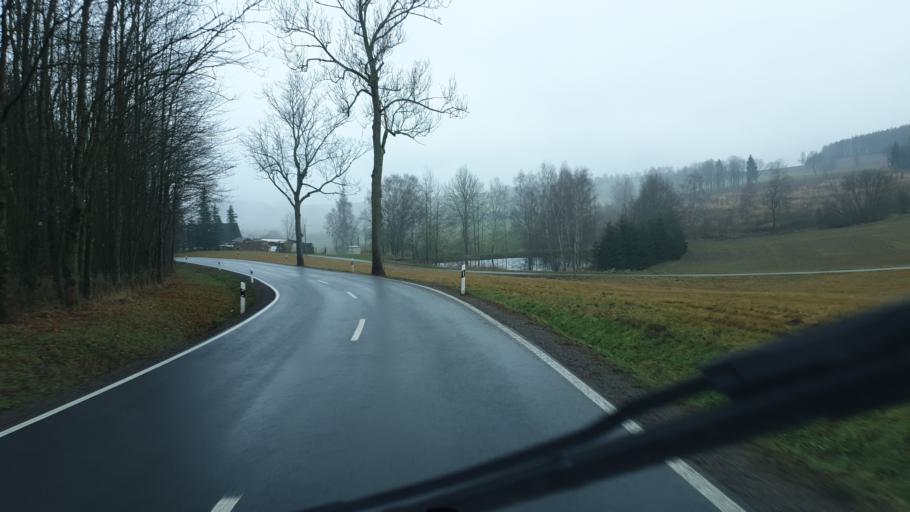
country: DE
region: Saxony
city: Neuhausen
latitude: 50.6908
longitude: 13.4603
